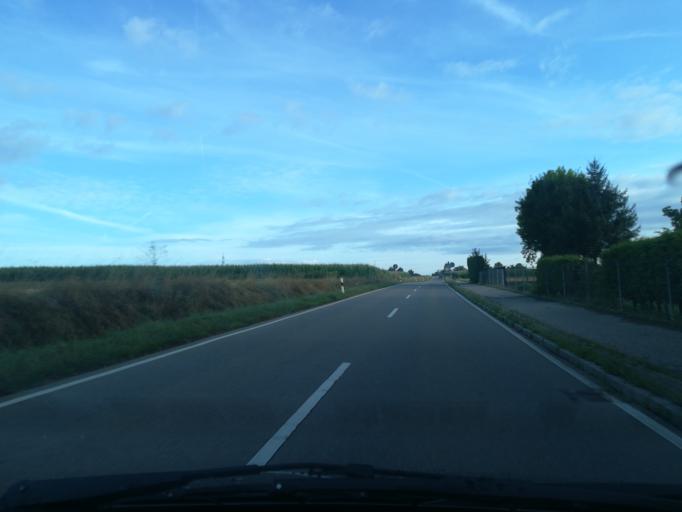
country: DE
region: Baden-Wuerttemberg
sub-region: Tuebingen Region
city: Sickenhausen
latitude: 48.5089
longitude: 9.1788
